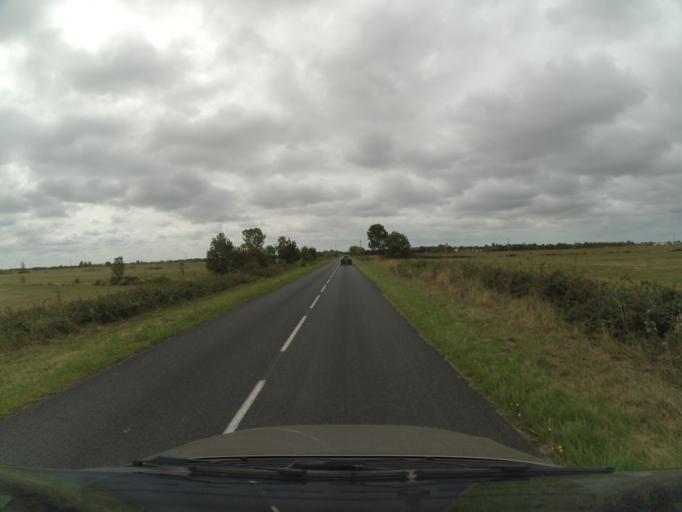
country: FR
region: Pays de la Loire
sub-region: Departement de la Vendee
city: Triaize
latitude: 46.4067
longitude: -1.2962
